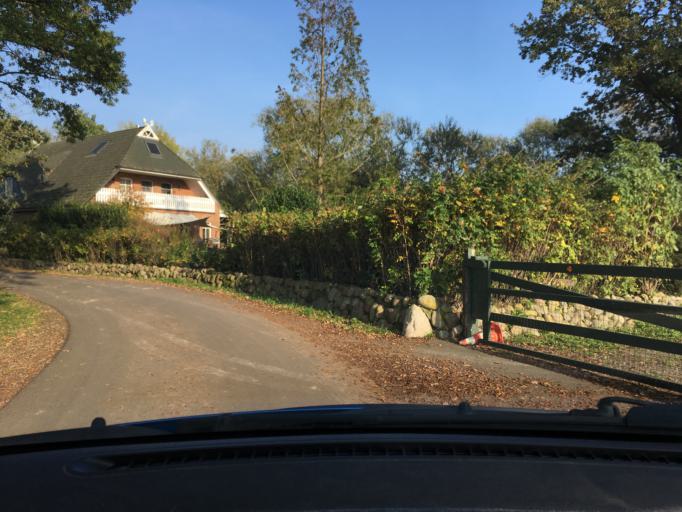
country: DE
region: Lower Saxony
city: Artlenburg
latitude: 53.3699
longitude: 10.4961
